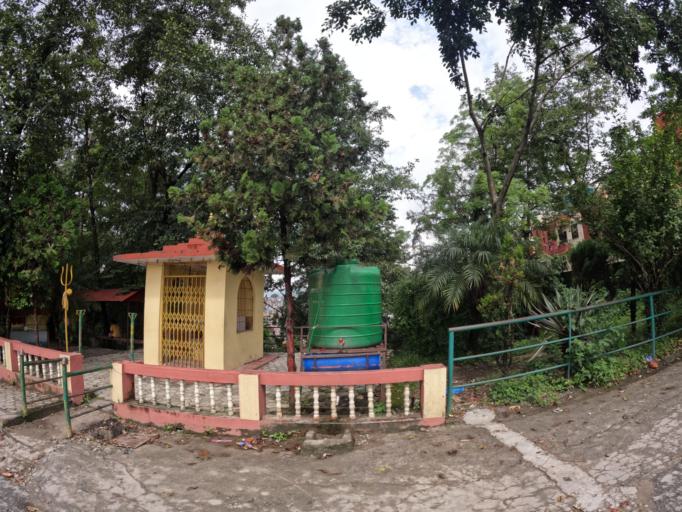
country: NP
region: Central Region
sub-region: Bagmati Zone
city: Kathmandu
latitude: 27.7494
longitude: 85.3195
